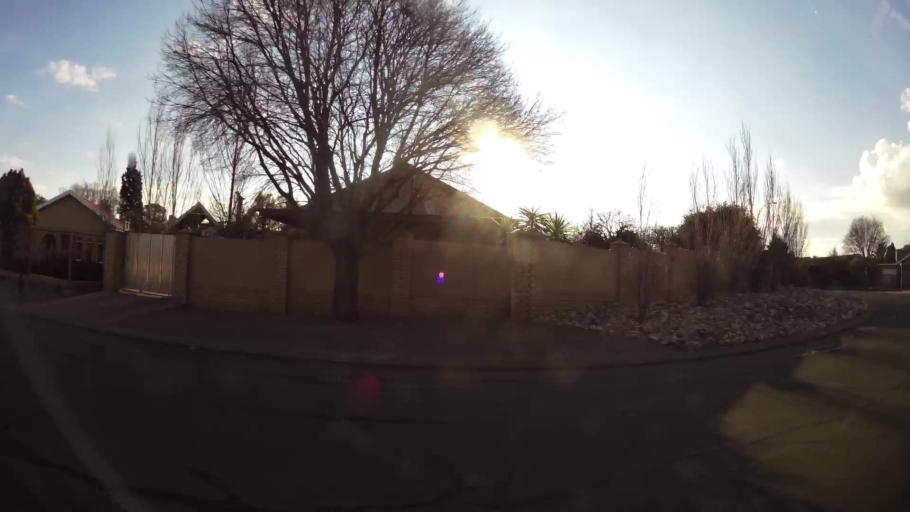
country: ZA
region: Orange Free State
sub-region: Mangaung Metropolitan Municipality
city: Bloemfontein
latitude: -29.1564
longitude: 26.1832
